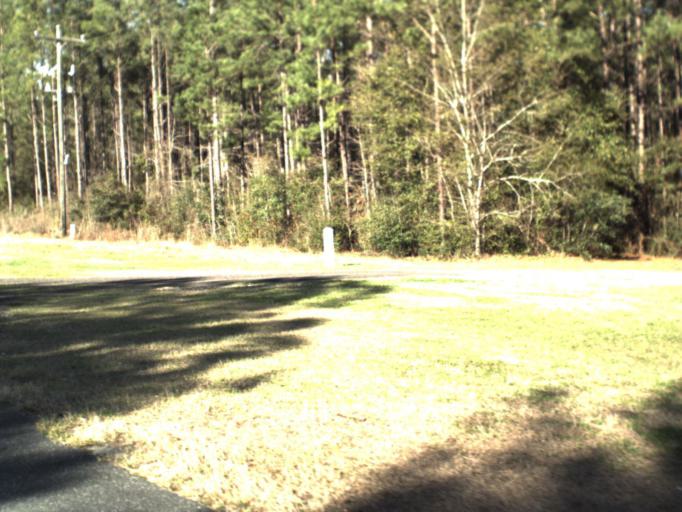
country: US
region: Florida
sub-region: Calhoun County
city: Blountstown
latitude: 30.5022
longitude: -85.2002
